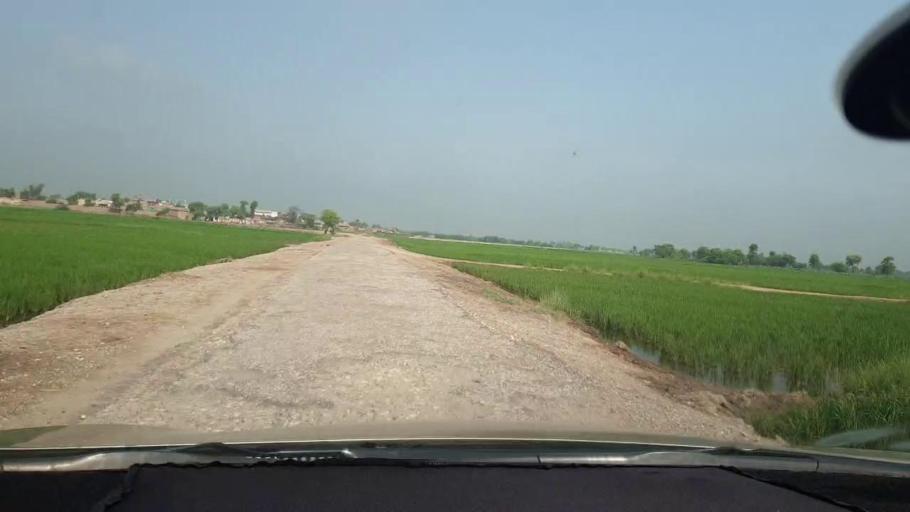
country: PK
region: Sindh
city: Kambar
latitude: 27.5406
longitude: 68.0509
